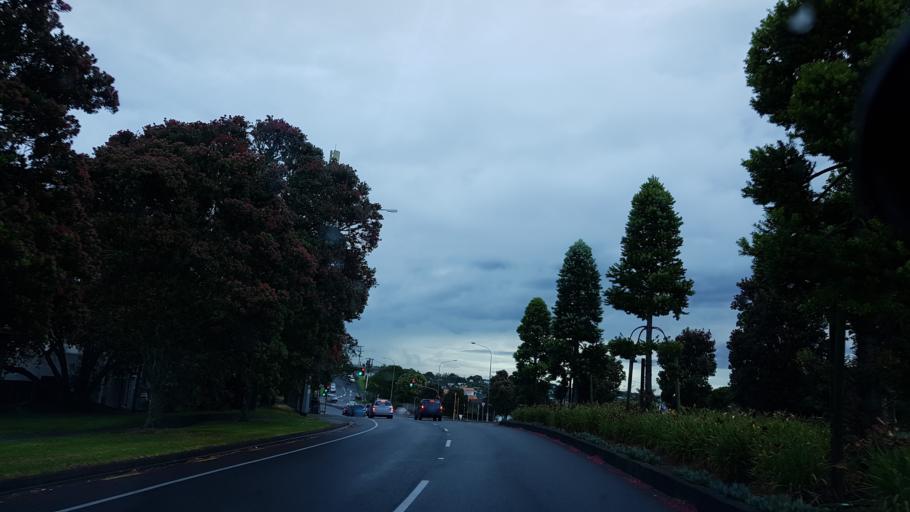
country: NZ
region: Auckland
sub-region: Auckland
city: North Shore
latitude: -36.7780
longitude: 174.7229
